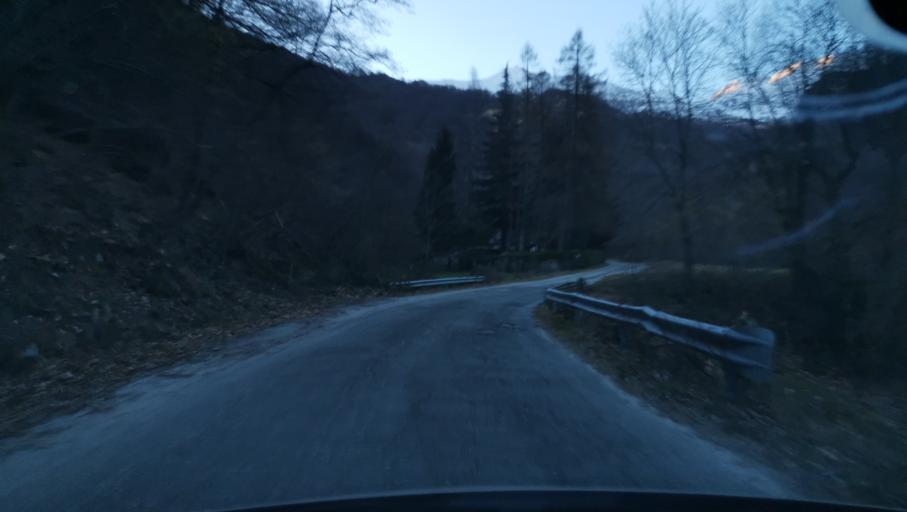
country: IT
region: Piedmont
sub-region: Provincia di Torino
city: Rora
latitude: 44.7722
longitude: 7.2052
